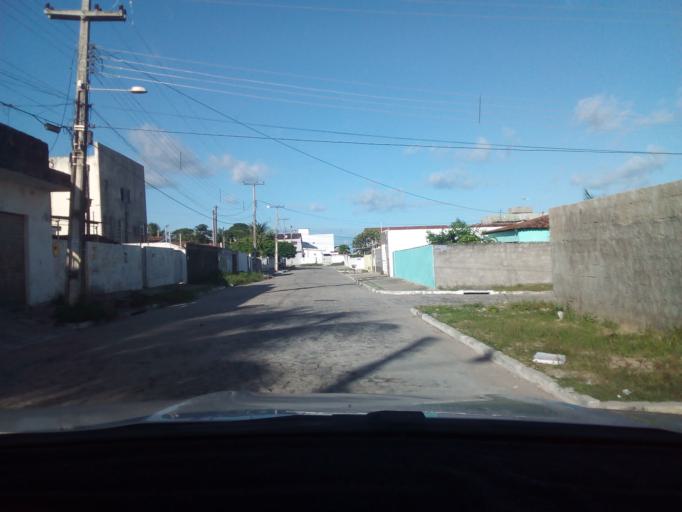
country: BR
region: Paraiba
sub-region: Joao Pessoa
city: Joao Pessoa
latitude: -7.1779
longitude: -34.8283
